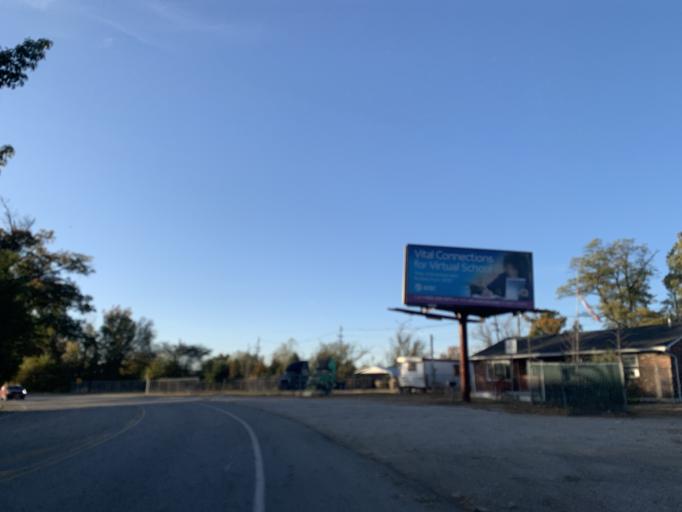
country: US
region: Kentucky
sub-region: Jefferson County
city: Shively
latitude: 38.2322
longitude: -85.8278
